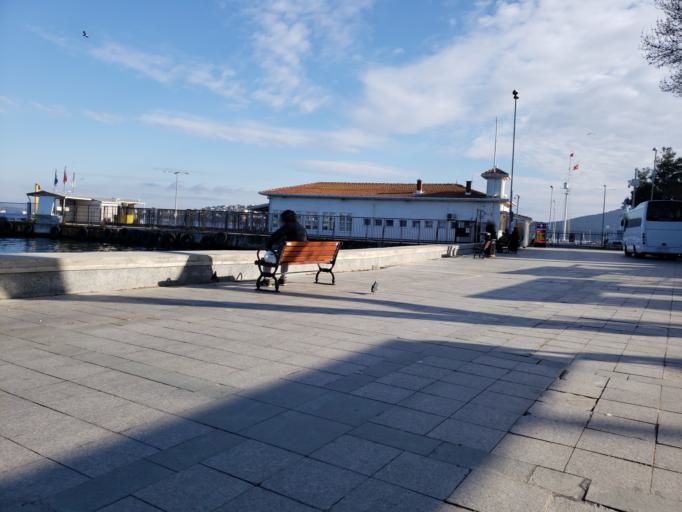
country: TR
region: Istanbul
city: Adalan
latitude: 40.8771
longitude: 29.1011
